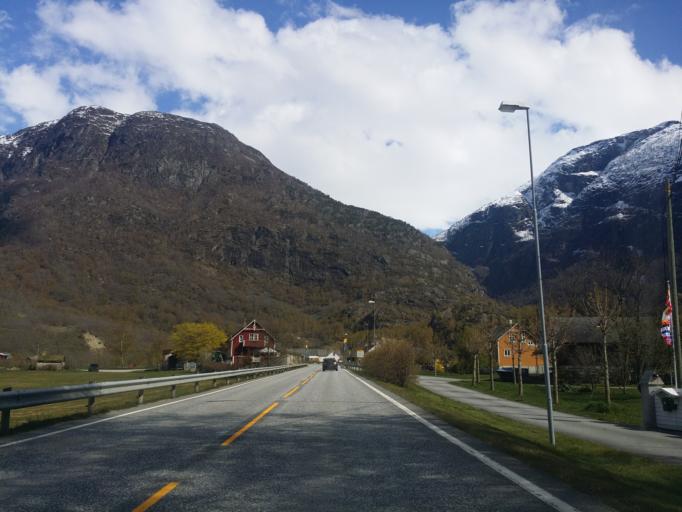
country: NO
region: Hordaland
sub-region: Eidfjord
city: Eidfjord
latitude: 60.4240
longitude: 7.1241
